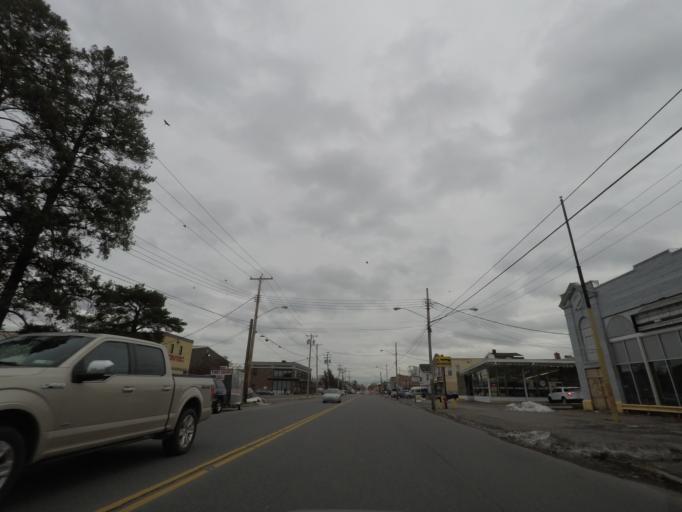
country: US
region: New York
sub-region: Schenectady County
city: Schenectady
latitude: 42.8026
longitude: -73.9292
